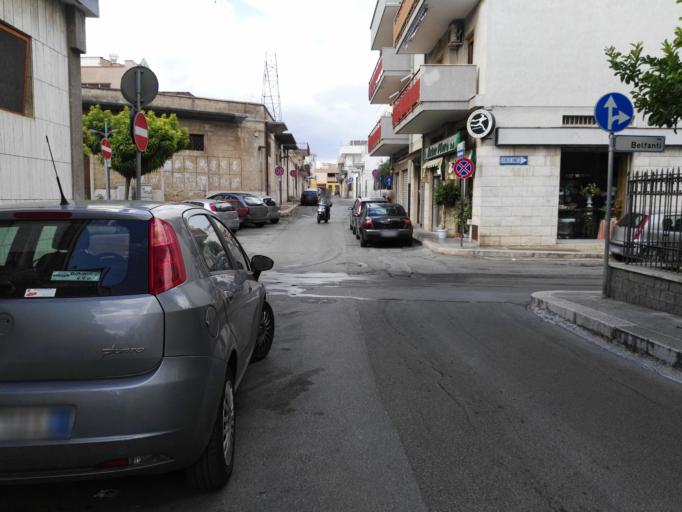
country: IT
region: Apulia
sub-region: Provincia di Bari
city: Triggiano
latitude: 41.0648
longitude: 16.9185
